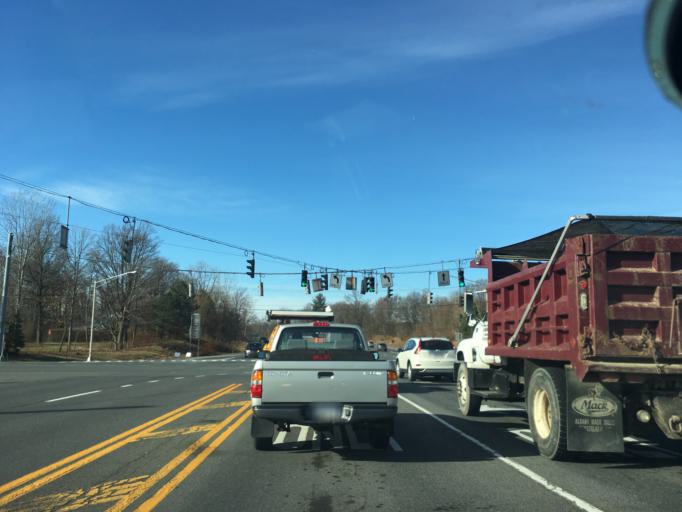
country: US
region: New York
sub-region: Rensselaer County
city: Hampton Manor
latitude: 42.6546
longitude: -73.6937
